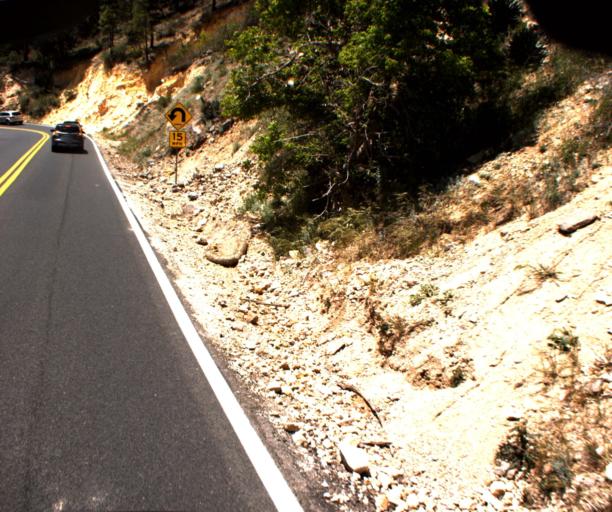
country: US
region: Arizona
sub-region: Coconino County
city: Kachina Village
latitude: 35.0257
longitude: -111.7403
